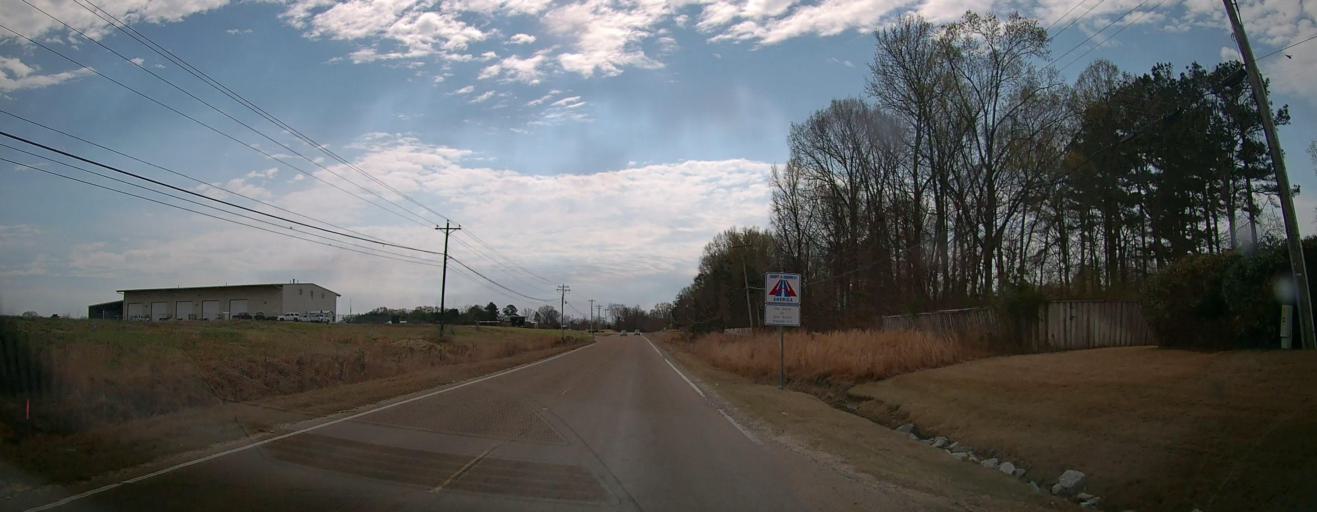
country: US
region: Mississippi
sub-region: De Soto County
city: Olive Branch
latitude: 34.9436
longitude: -89.8072
